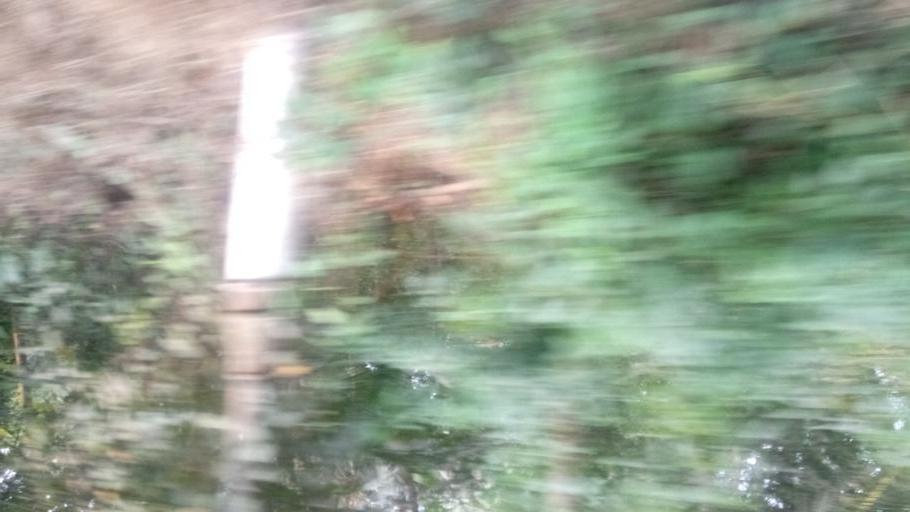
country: IN
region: Goa
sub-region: South Goa
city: Varca
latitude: 15.2212
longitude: 73.9506
